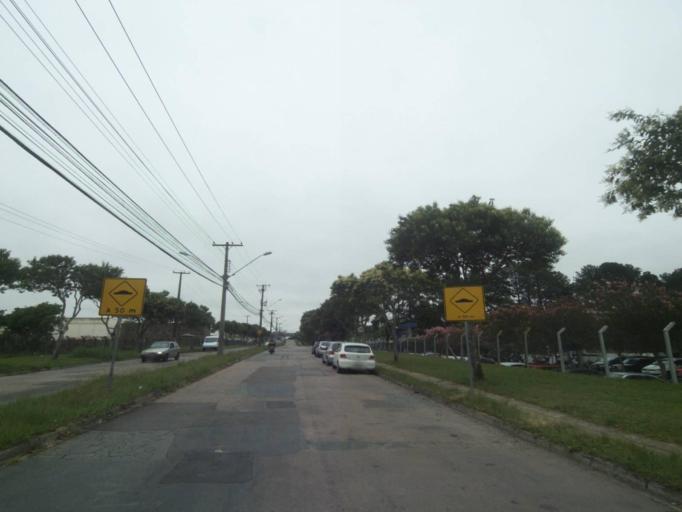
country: BR
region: Parana
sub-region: Sao Jose Dos Pinhais
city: Sao Jose dos Pinhais
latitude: -25.5310
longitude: -49.3147
